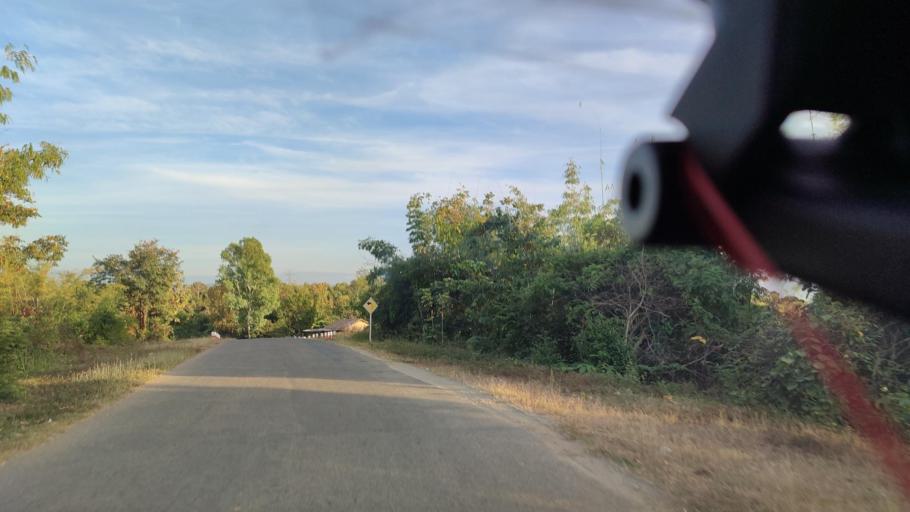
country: MM
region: Mandalay
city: Nay Pyi Taw
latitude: 19.9843
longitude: 95.9598
